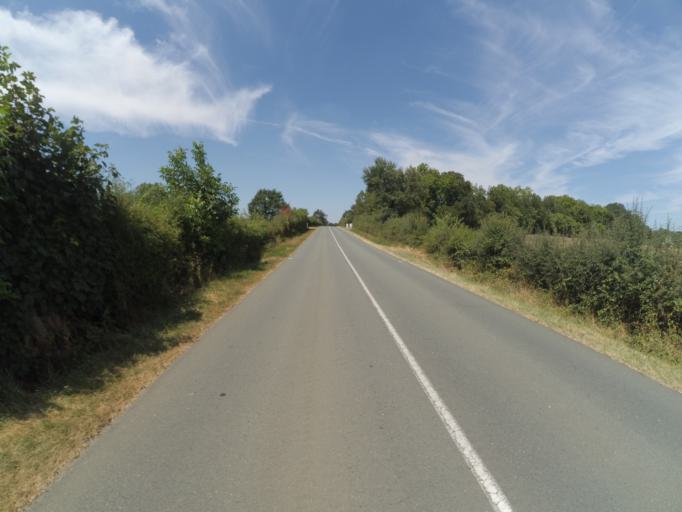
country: FR
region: Poitou-Charentes
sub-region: Departement de la Vienne
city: Usson-du-Poitou
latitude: 46.3071
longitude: 0.4978
